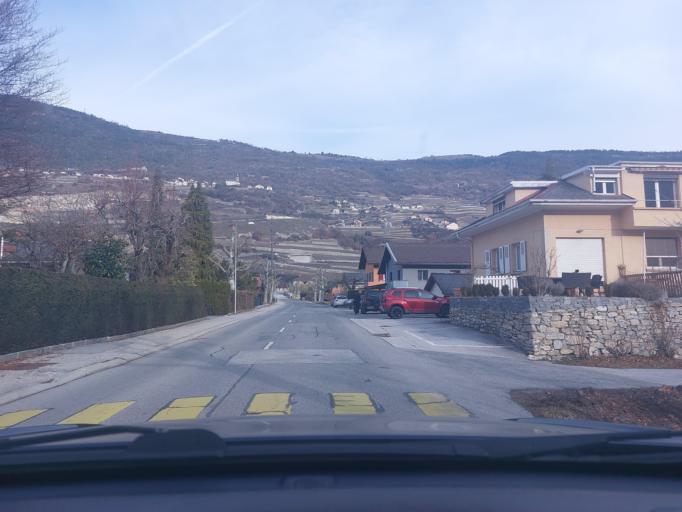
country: CH
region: Valais
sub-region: Sierre District
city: Grone
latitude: 46.2622
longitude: 7.4615
